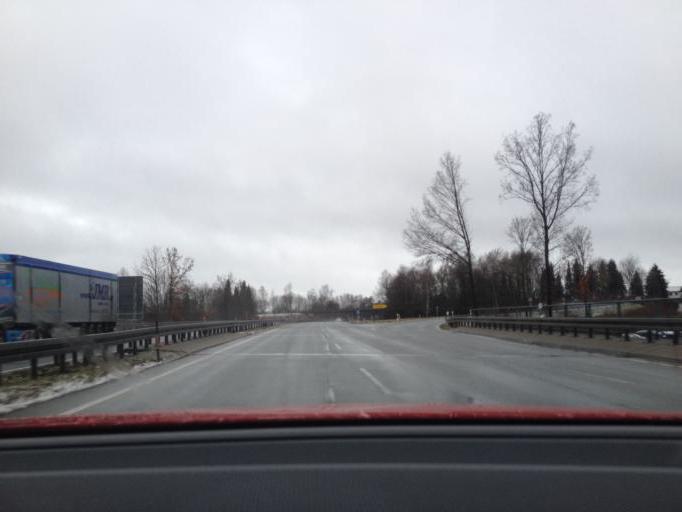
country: DE
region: Bavaria
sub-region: Upper Franconia
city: Hof
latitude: 50.2891
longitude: 11.9188
